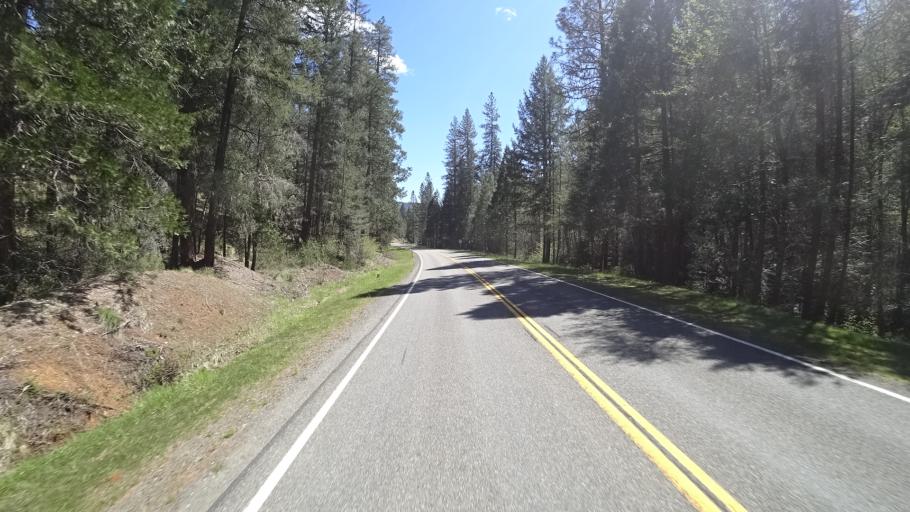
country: US
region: California
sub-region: Trinity County
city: Weaverville
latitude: 40.7709
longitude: -122.8913
